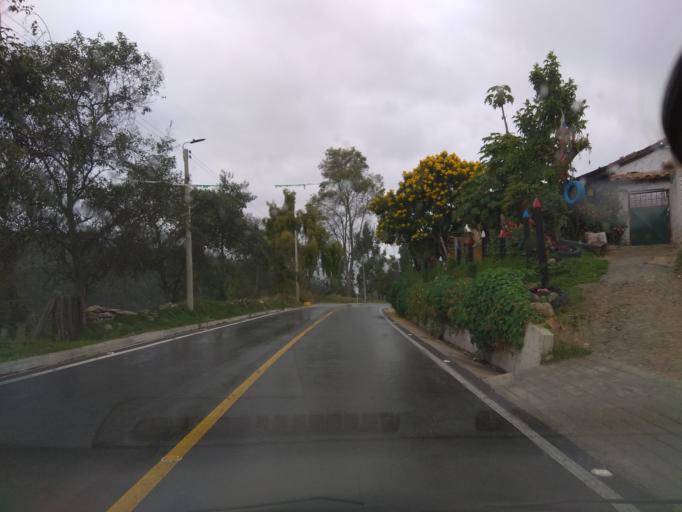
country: CO
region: Boyaca
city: Mongui
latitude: 5.7314
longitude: -72.8513
